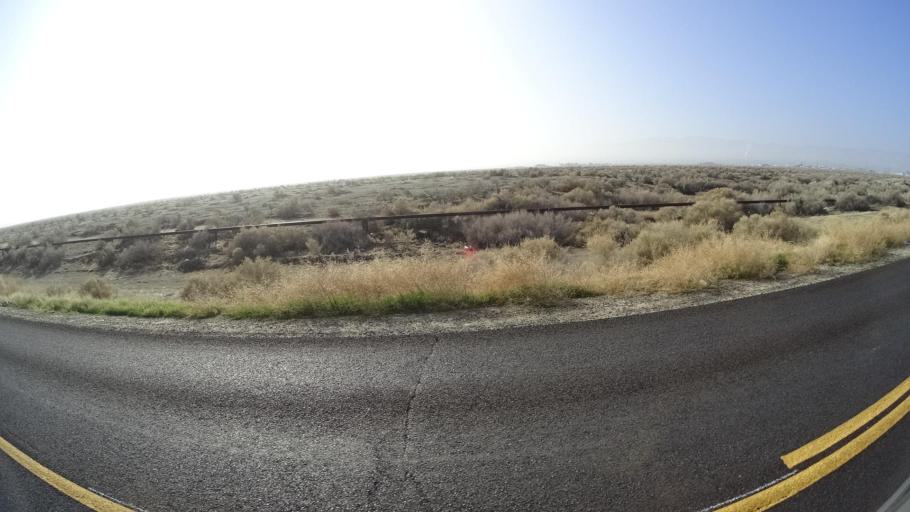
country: US
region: California
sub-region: Kern County
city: Ford City
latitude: 35.1805
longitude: -119.5046
